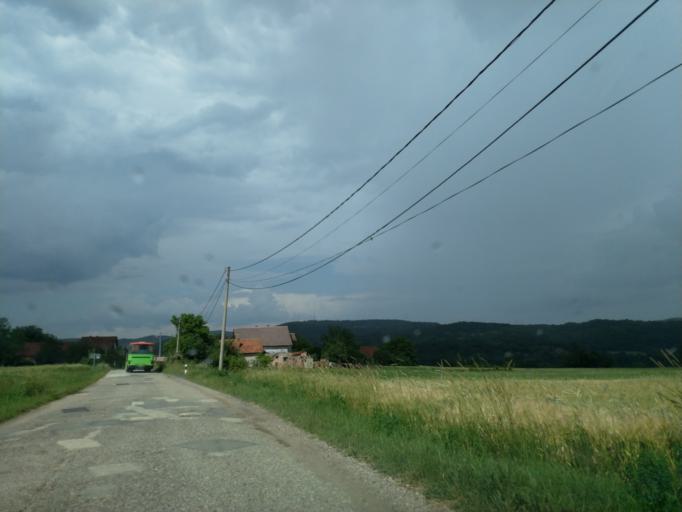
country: RS
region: Central Serbia
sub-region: Borski Okrug
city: Bor
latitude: 44.0025
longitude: 21.9801
